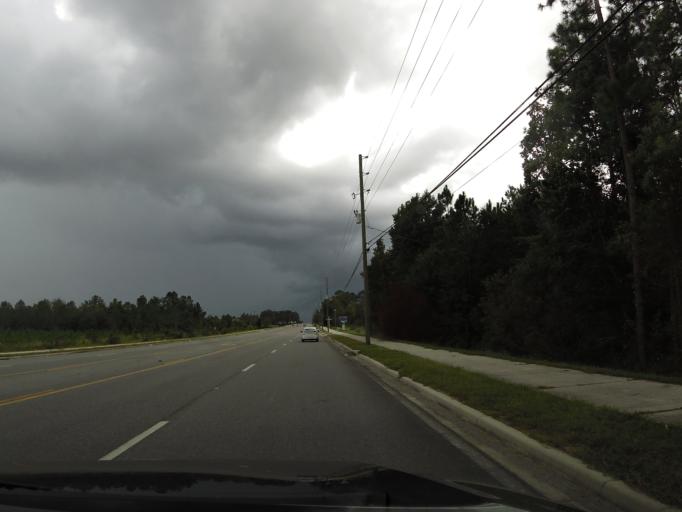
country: US
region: Florida
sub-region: Clay County
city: Asbury Lake
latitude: 30.0611
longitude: -81.8097
